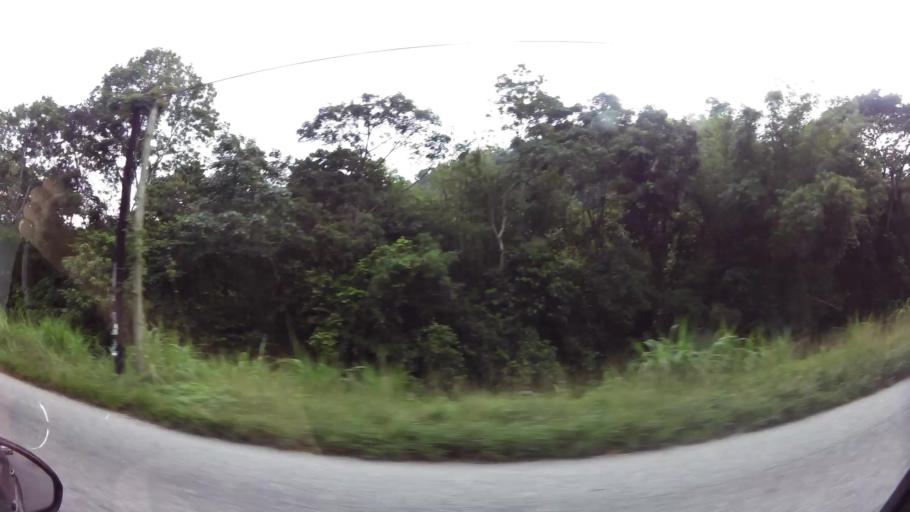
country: TT
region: San Juan/Laventille
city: Laventille
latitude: 10.6898
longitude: -61.4575
